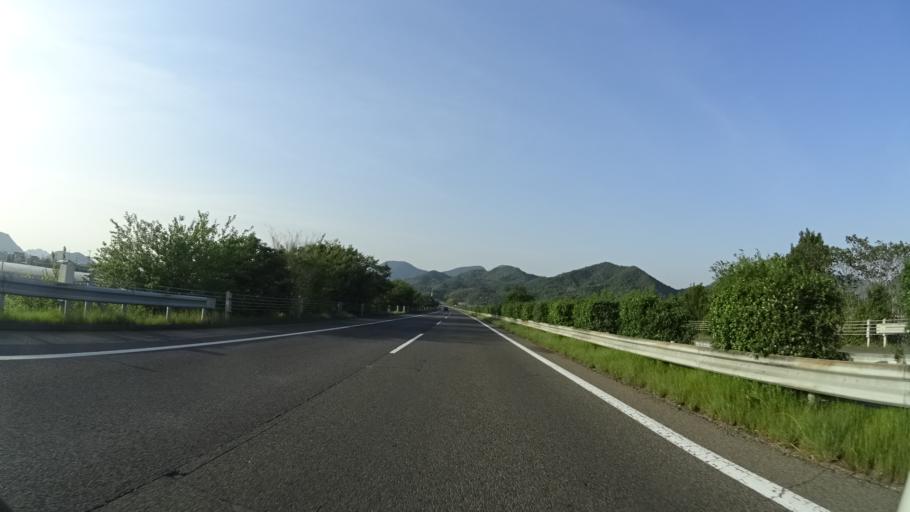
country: JP
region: Kagawa
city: Kan'onjicho
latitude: 34.1662
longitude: 133.7316
